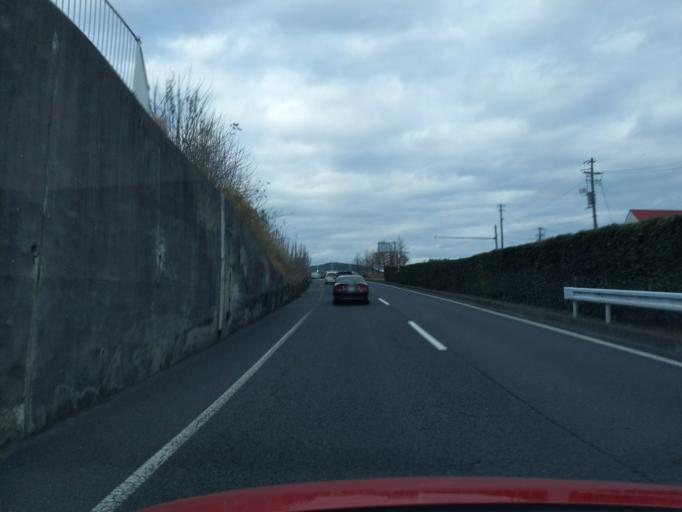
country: JP
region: Aichi
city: Kasugai
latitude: 35.2929
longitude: 137.0193
